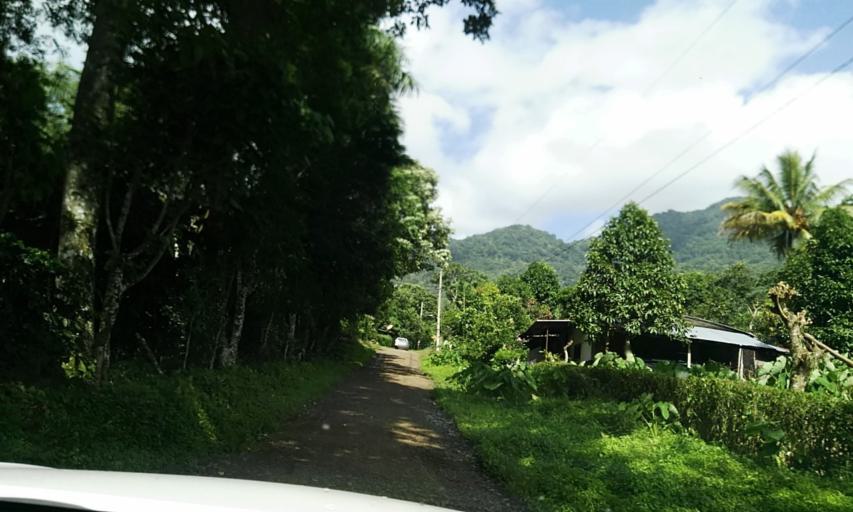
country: NI
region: Matagalpa
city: San Ramon
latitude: 12.9971
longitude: -85.8681
